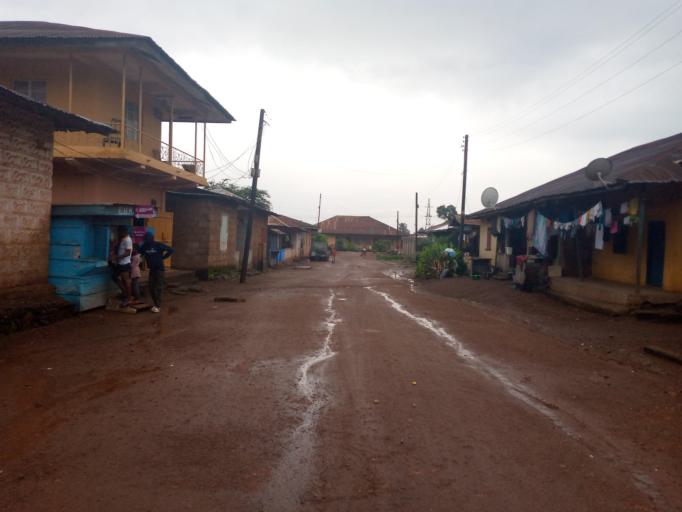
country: SL
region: Eastern Province
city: Kenema
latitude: 7.8829
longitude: -11.1871
